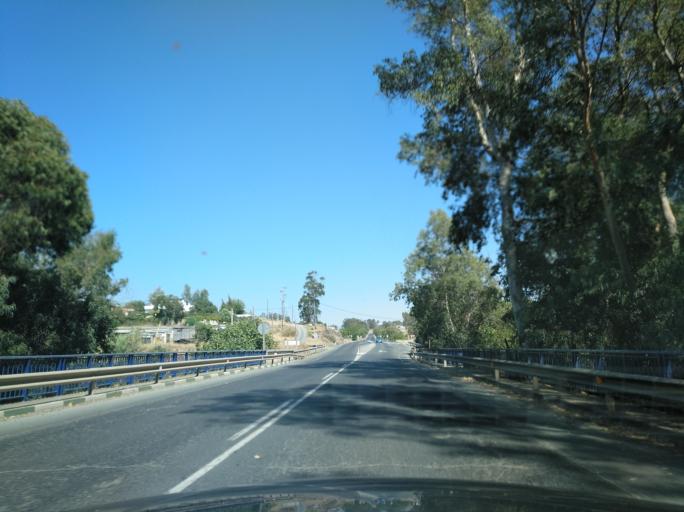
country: ES
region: Andalusia
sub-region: Provincia de Huelva
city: Gibraleon
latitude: 37.3795
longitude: -6.9779
